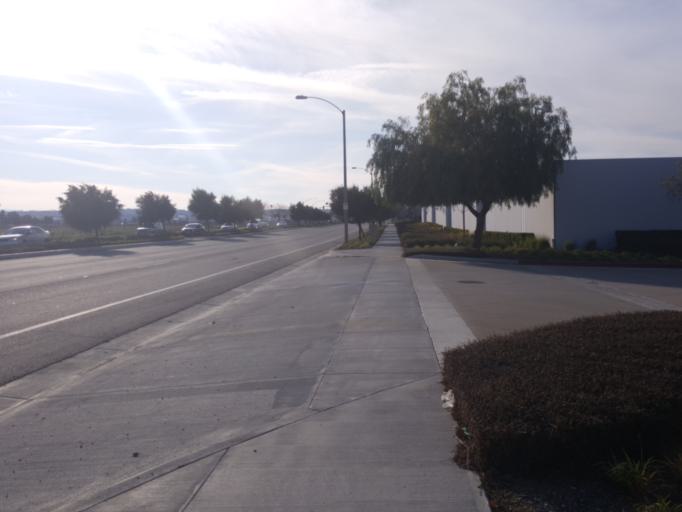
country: US
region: California
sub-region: Riverside County
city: March Air Force Base
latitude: 33.9104
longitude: -117.2633
